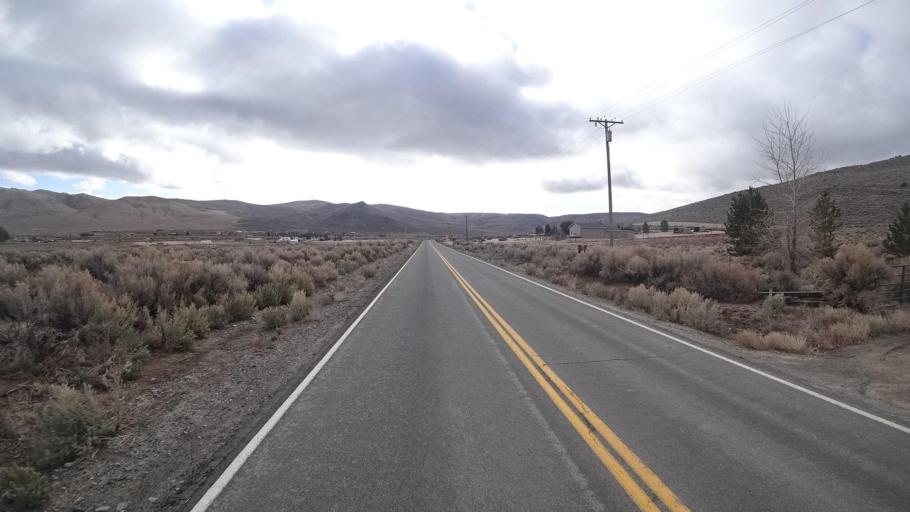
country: US
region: Nevada
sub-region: Washoe County
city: Cold Springs
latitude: 39.8626
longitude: -119.9398
